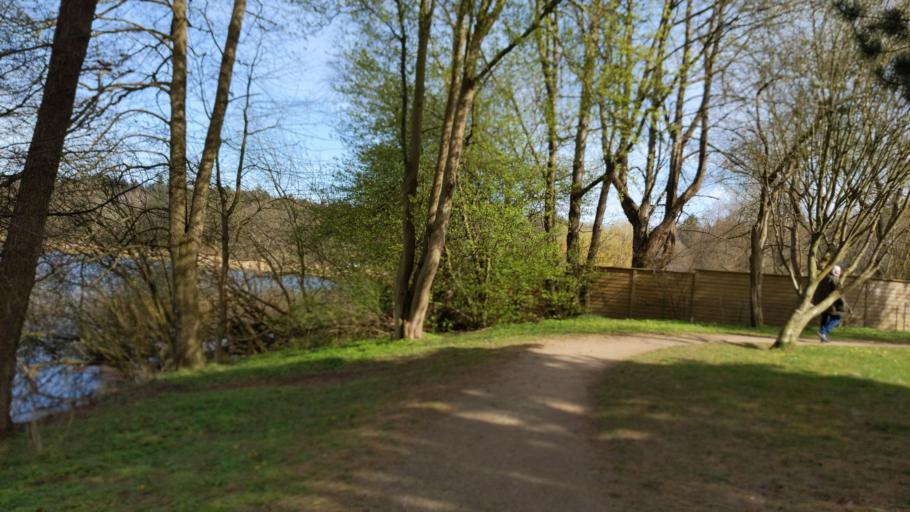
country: DE
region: Schleswig-Holstein
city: Susel
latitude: 54.0262
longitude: 10.6955
